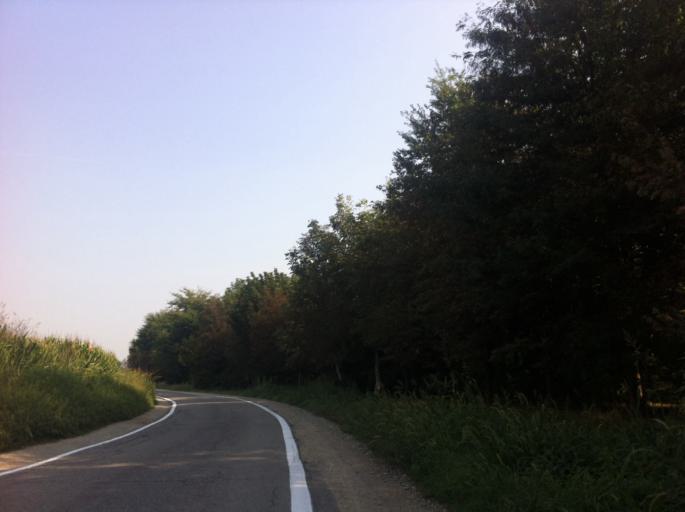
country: IT
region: Lombardy
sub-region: Provincia di Lodi
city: Quartiano
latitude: 45.3491
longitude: 9.4127
